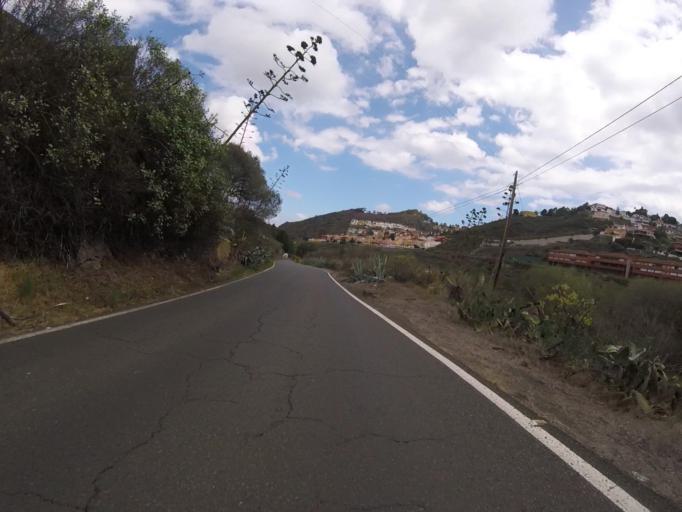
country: ES
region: Canary Islands
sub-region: Provincia de Las Palmas
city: Santa Brigida
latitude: 28.0478
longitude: -15.4820
